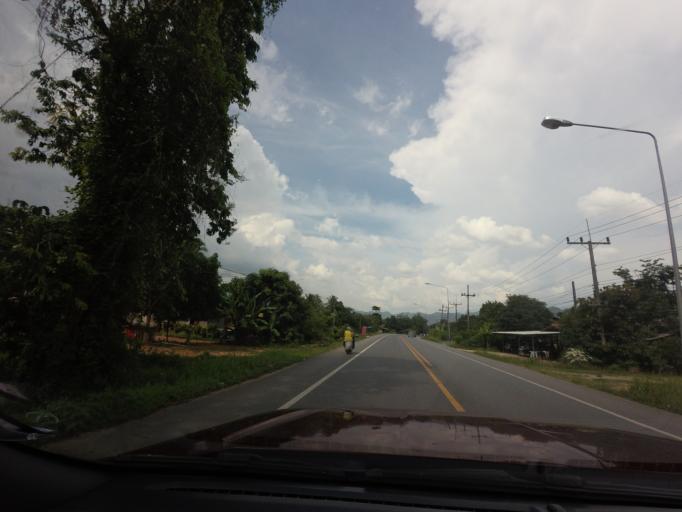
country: TH
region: Yala
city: Ban Nang Sata
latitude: 6.2570
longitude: 101.2426
